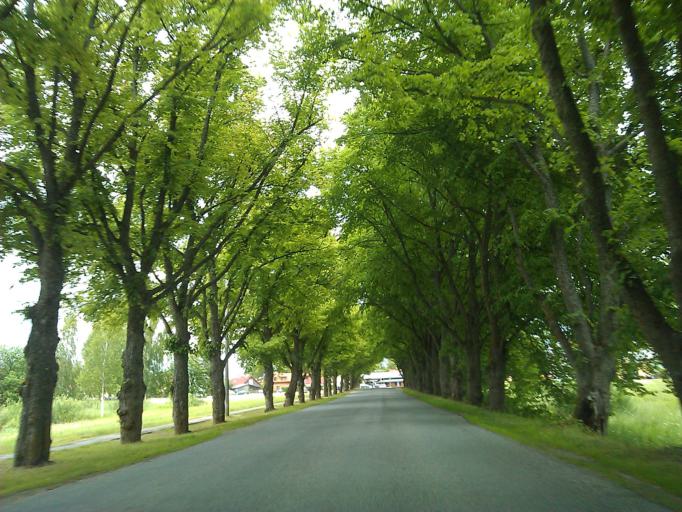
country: LV
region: Kuldigas Rajons
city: Kuldiga
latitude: 56.9656
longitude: 21.9549
